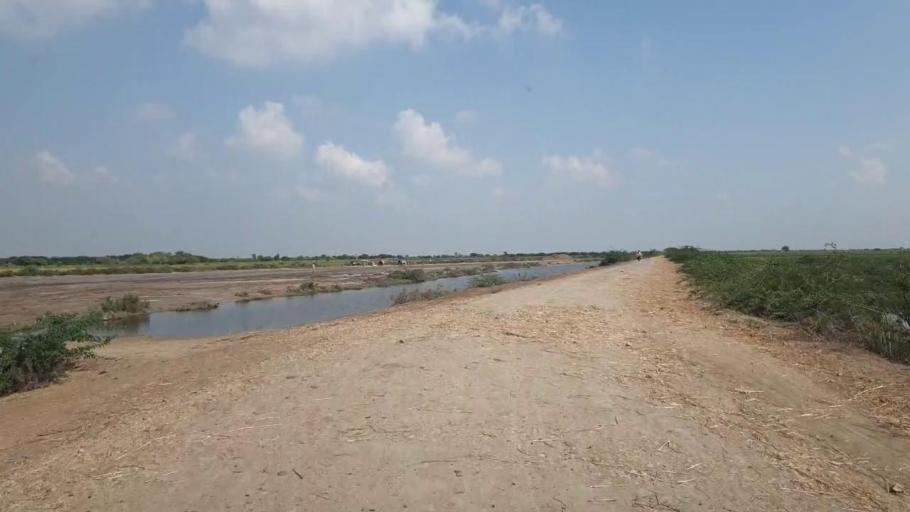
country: PK
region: Sindh
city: Badin
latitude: 24.4731
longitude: 68.5907
